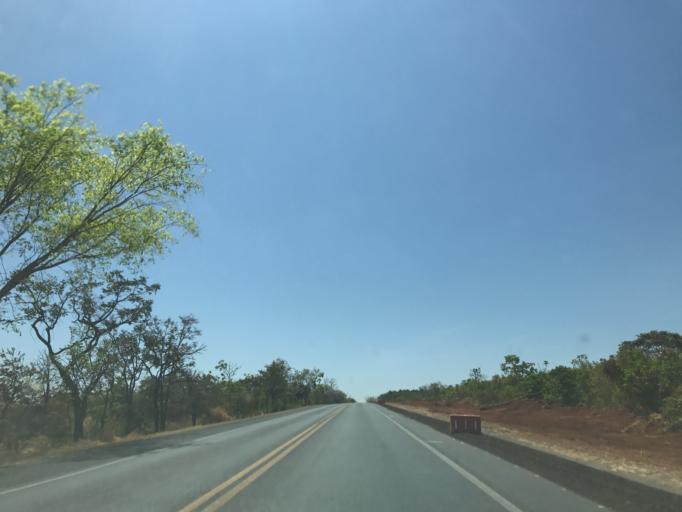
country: BR
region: Minas Gerais
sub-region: Prata
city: Prata
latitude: -19.4076
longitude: -48.8951
